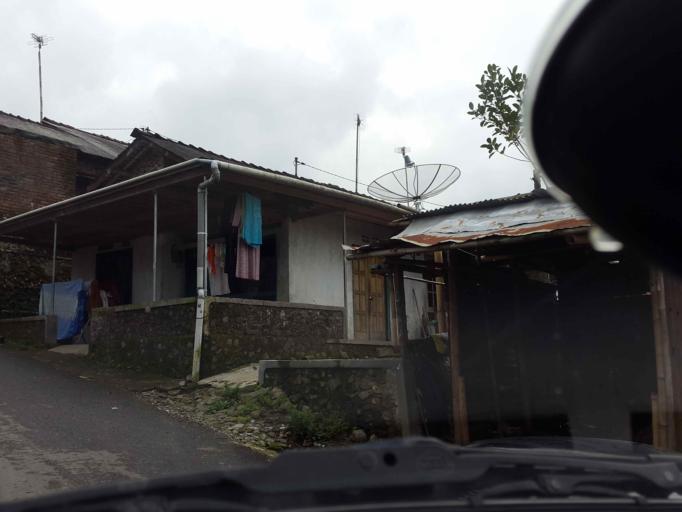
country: ID
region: Central Java
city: Wonosobo
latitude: -7.3718
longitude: 109.9875
